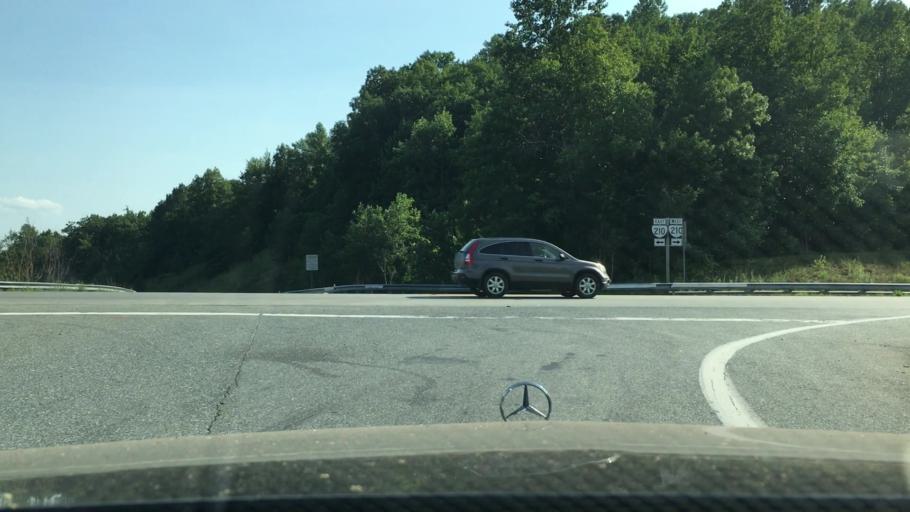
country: US
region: Virginia
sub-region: Amherst County
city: Madison Heights
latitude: 37.4085
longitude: -79.0857
